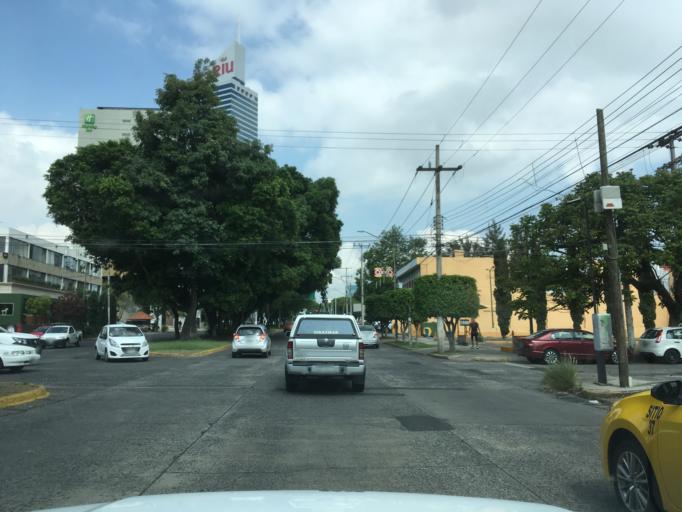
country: MX
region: Jalisco
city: Guadalajara
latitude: 20.6666
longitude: -103.3900
